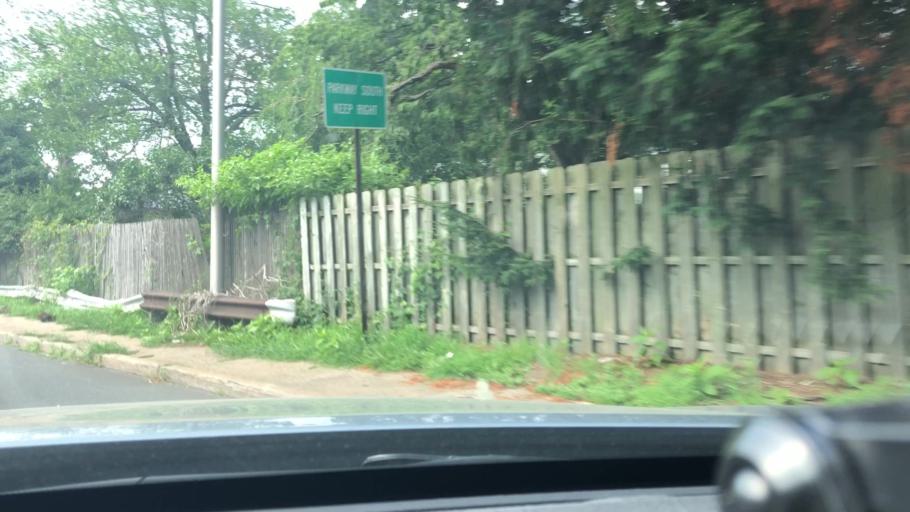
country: US
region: New Jersey
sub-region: Union County
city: Winfield
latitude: 40.6447
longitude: -74.2901
